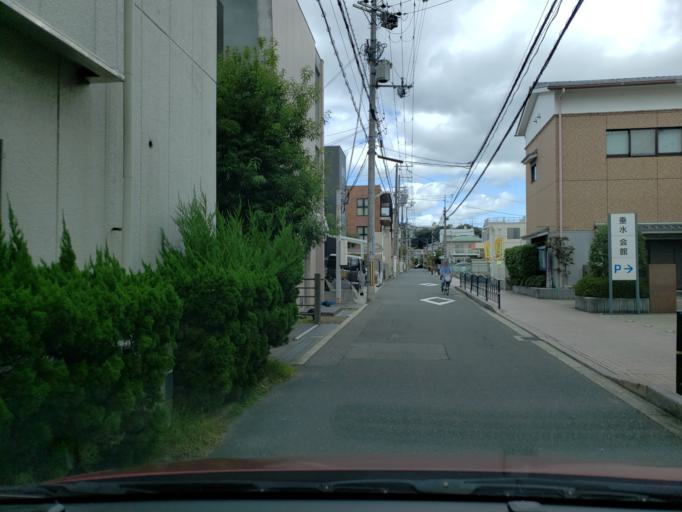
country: JP
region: Osaka
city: Suita
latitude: 34.7622
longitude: 135.5053
